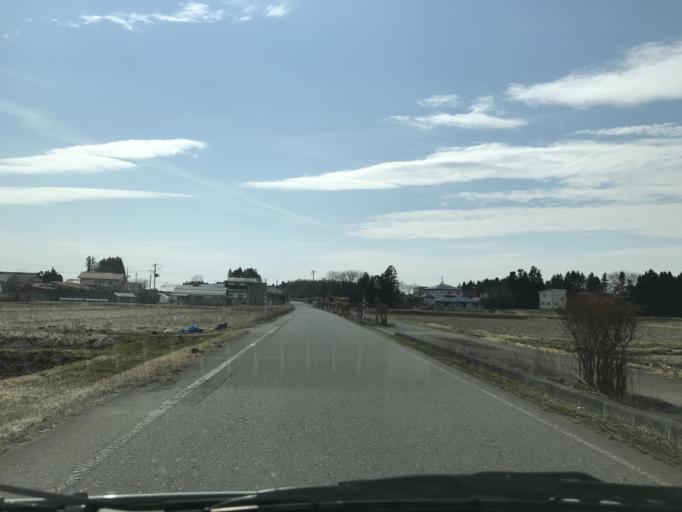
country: JP
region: Iwate
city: Mizusawa
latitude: 39.1261
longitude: 141.0707
